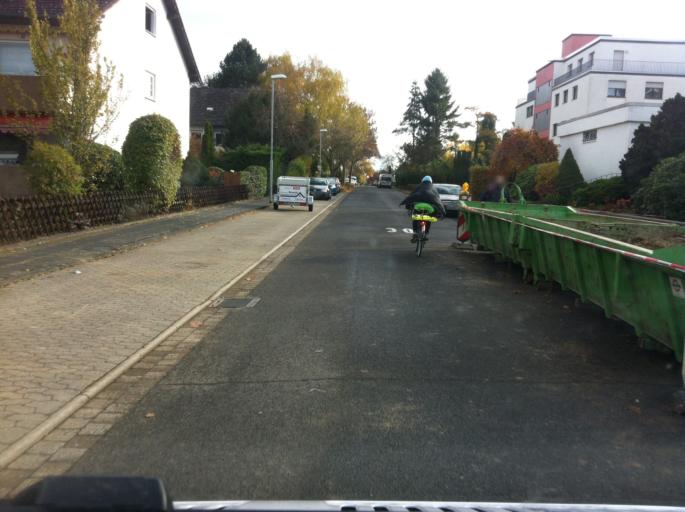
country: DE
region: North Rhine-Westphalia
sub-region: Regierungsbezirk Koln
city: Rheinbach
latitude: 50.6172
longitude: 6.9379
